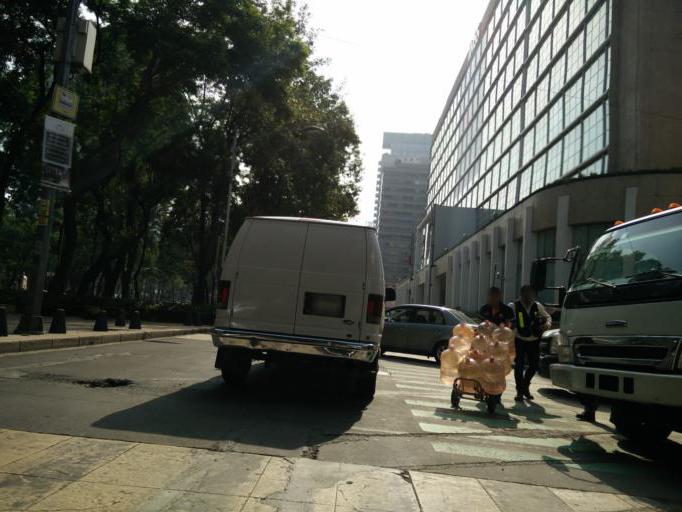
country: MX
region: Mexico City
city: Polanco
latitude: 19.4235
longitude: -99.1743
